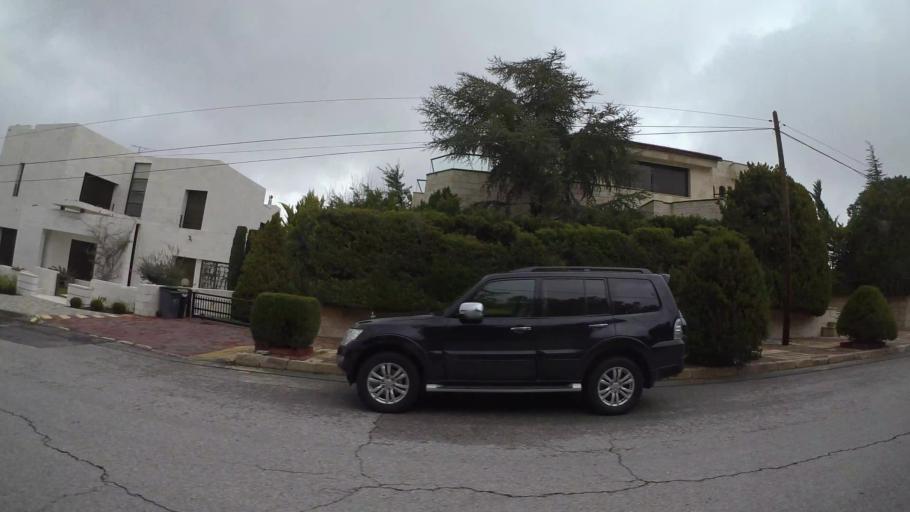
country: JO
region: Amman
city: Al Bunayyat ash Shamaliyah
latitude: 31.9384
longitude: 35.8822
